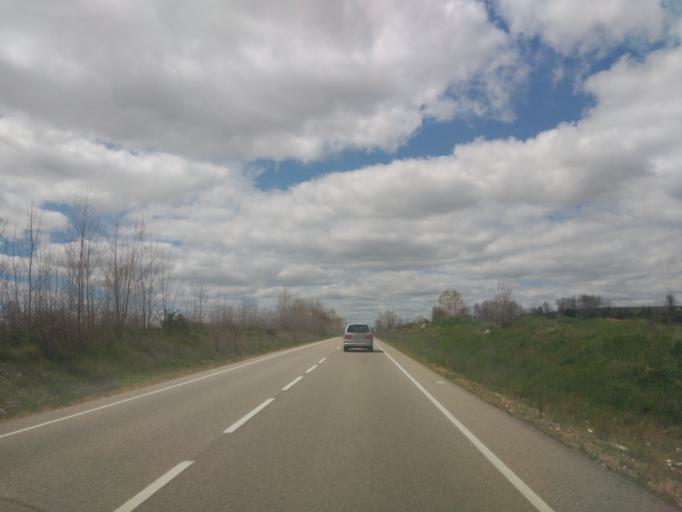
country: ES
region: Castille and Leon
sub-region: Provincia de Salamanca
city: Valverdon
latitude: 41.0486
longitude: -5.7769
